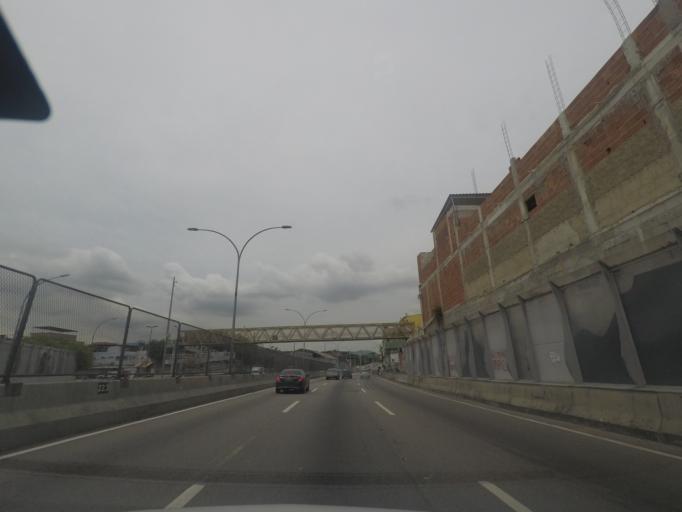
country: BR
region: Rio de Janeiro
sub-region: Rio De Janeiro
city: Rio de Janeiro
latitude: -22.8682
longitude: -43.2416
